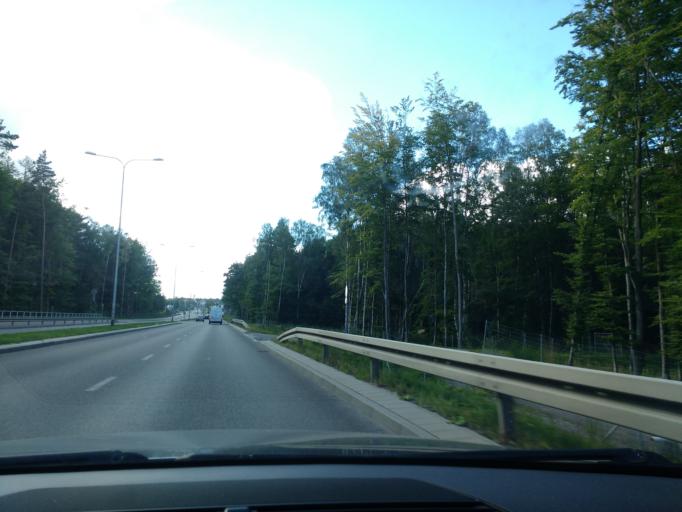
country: PL
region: Pomeranian Voivodeship
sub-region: Gdynia
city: Wielki Kack
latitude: 54.4995
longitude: 18.4784
